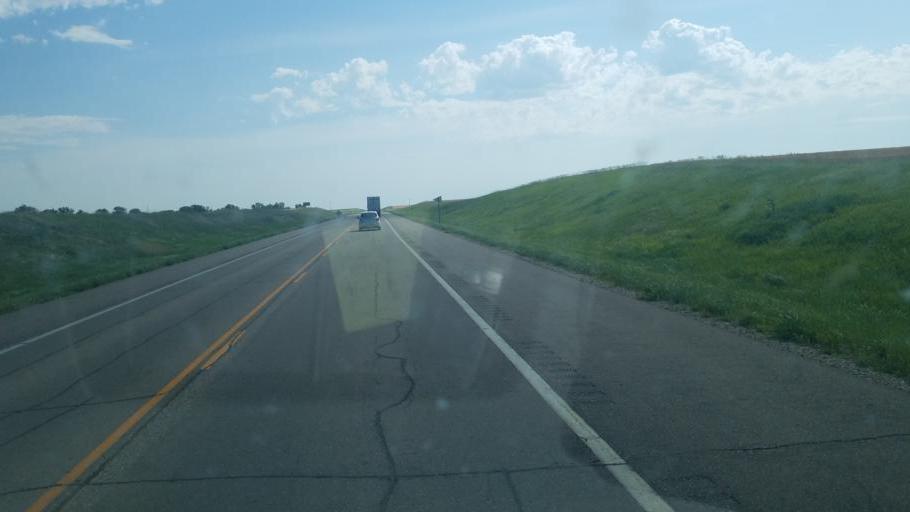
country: US
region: Kansas
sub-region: Ellsworth County
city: Ellsworth
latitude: 38.7593
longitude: -98.2099
